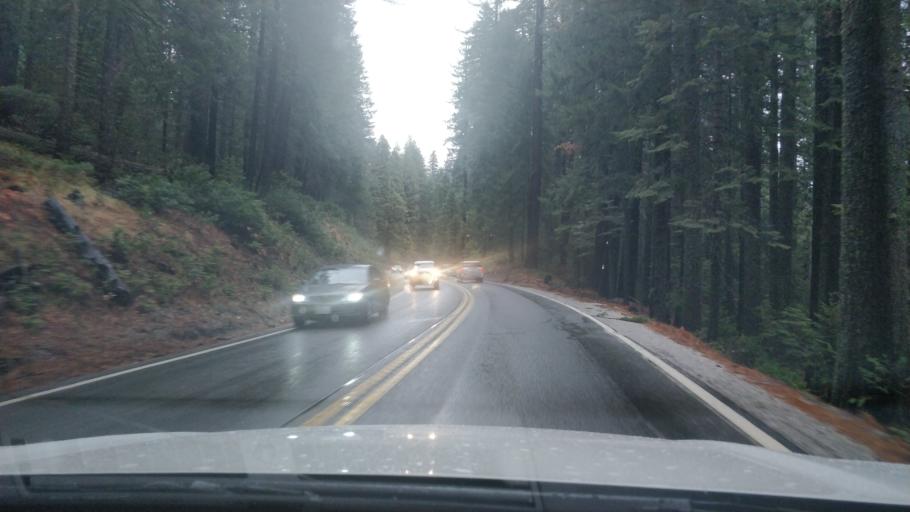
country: US
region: California
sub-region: Nevada County
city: Nevada City
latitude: 39.3184
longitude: -120.7940
